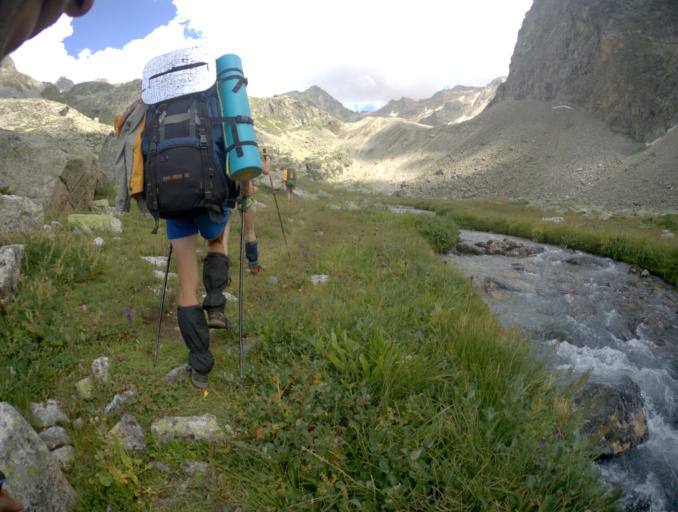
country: RU
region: Karachayevo-Cherkesiya
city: Uchkulan
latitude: 43.2859
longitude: 42.0872
